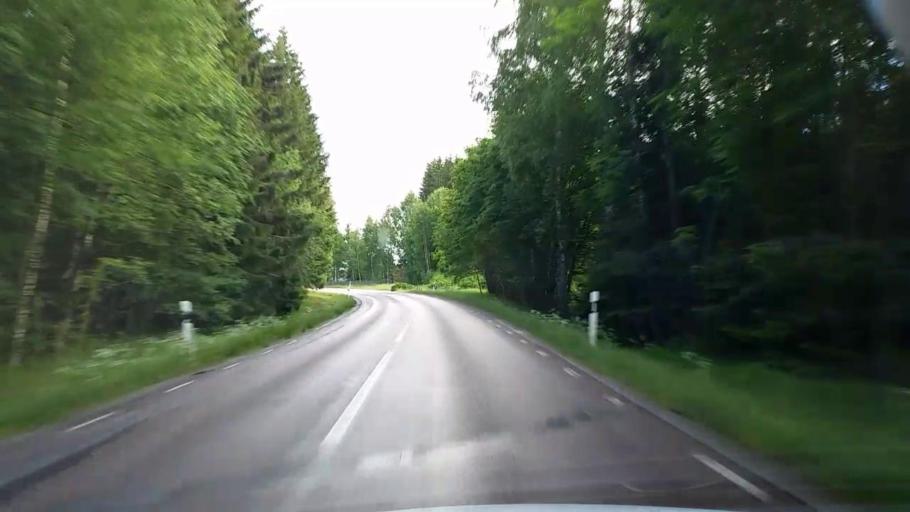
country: SE
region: Vaestmanland
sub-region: Fagersta Kommun
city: Fagersta
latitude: 59.9539
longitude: 15.7853
